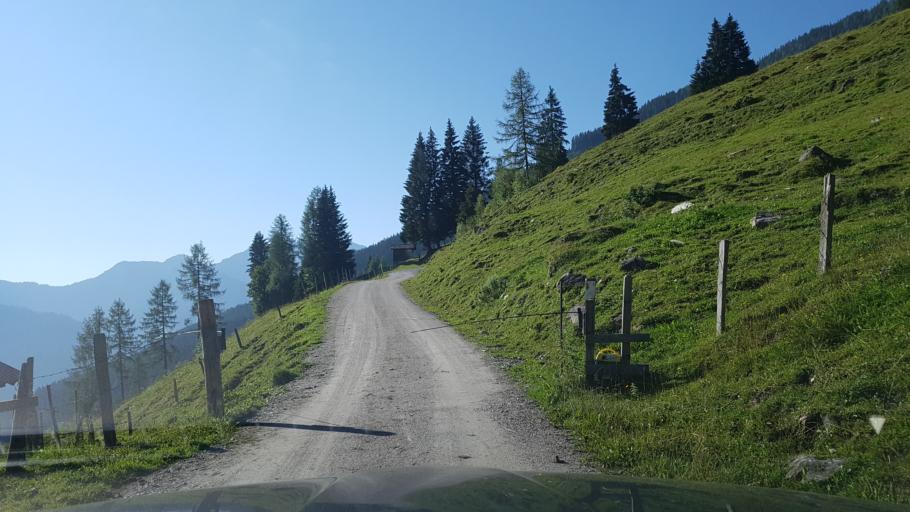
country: AT
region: Salzburg
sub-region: Politischer Bezirk Sankt Johann im Pongau
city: Dorfgastein
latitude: 47.2476
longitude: 13.0748
